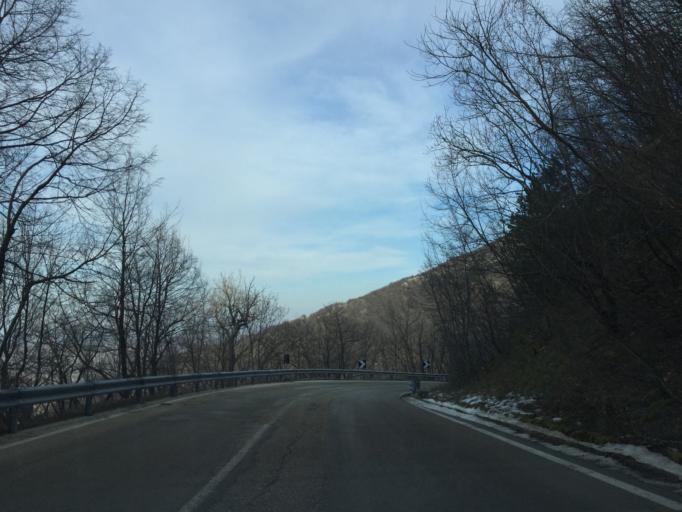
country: IT
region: Molise
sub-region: Provincia di Campobasso
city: San Massimo
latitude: 41.4771
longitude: 14.4164
